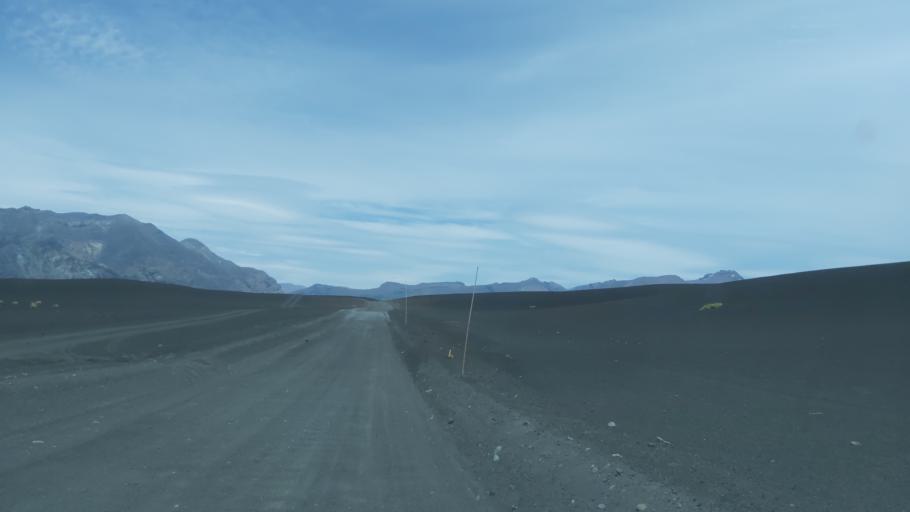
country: AR
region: Neuquen
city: Andacollo
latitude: -37.4329
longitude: -71.2858
